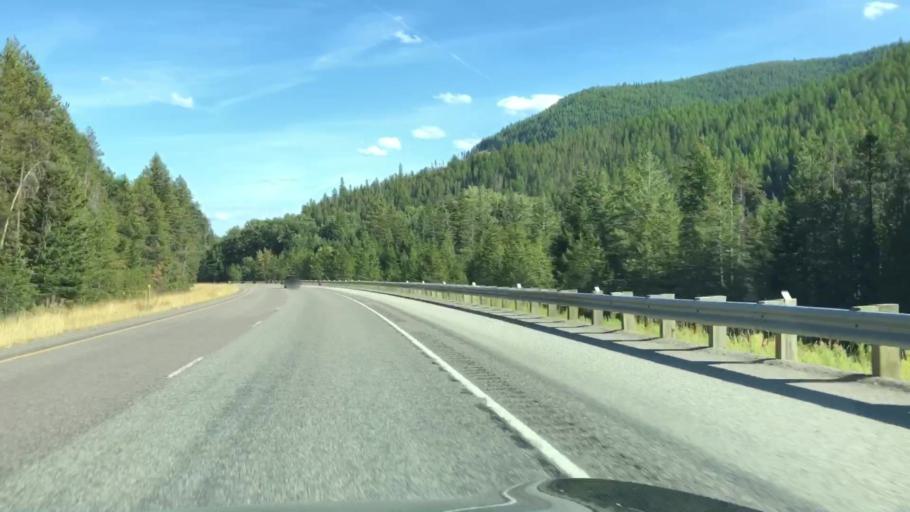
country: US
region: Montana
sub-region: Sanders County
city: Thompson Falls
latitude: 47.4055
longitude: -115.4883
